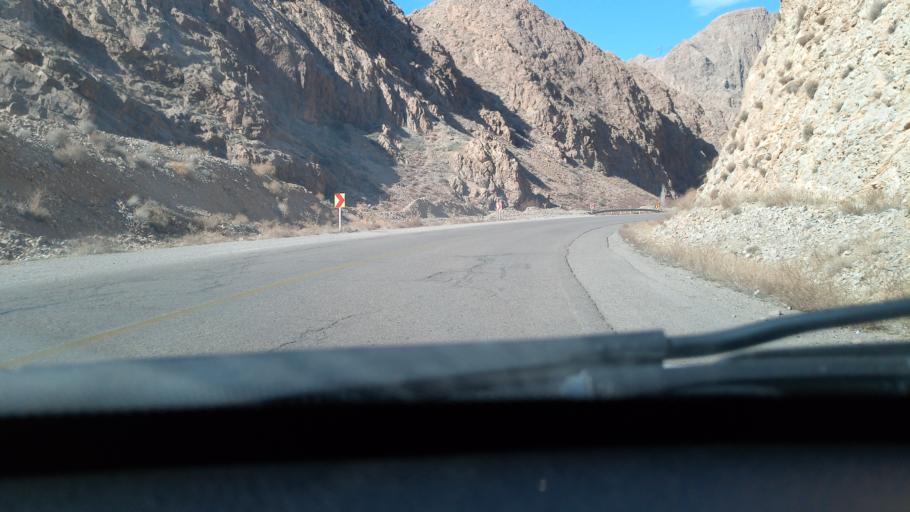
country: IR
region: Khorasan-e Shomali
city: Esfarayen
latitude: 37.1716
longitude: 57.4230
